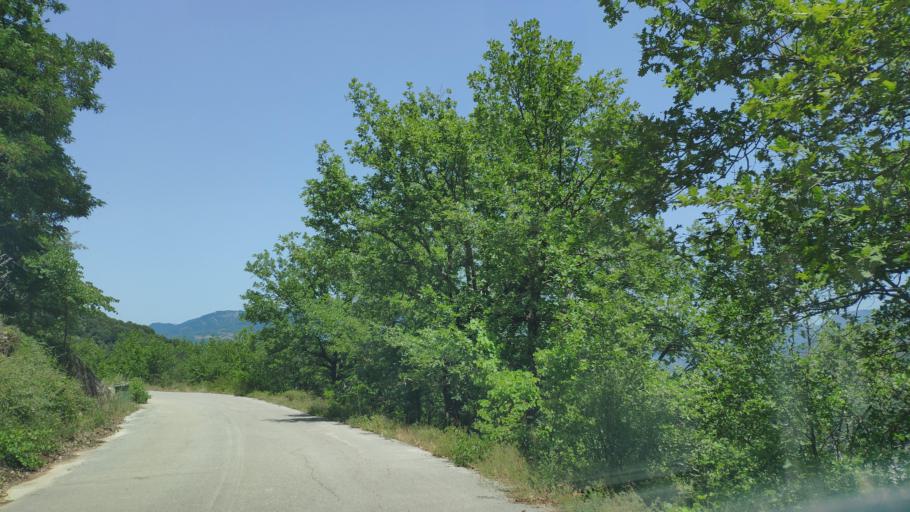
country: GR
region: Epirus
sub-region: Nomos Artas
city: Ano Kalentini
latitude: 39.1988
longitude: 21.3435
